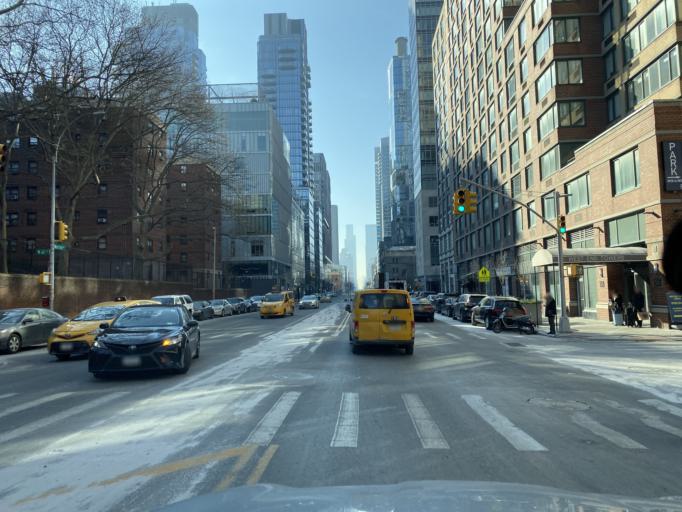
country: US
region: New Jersey
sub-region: Hudson County
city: Guttenberg
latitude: 40.7736
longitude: -73.9891
